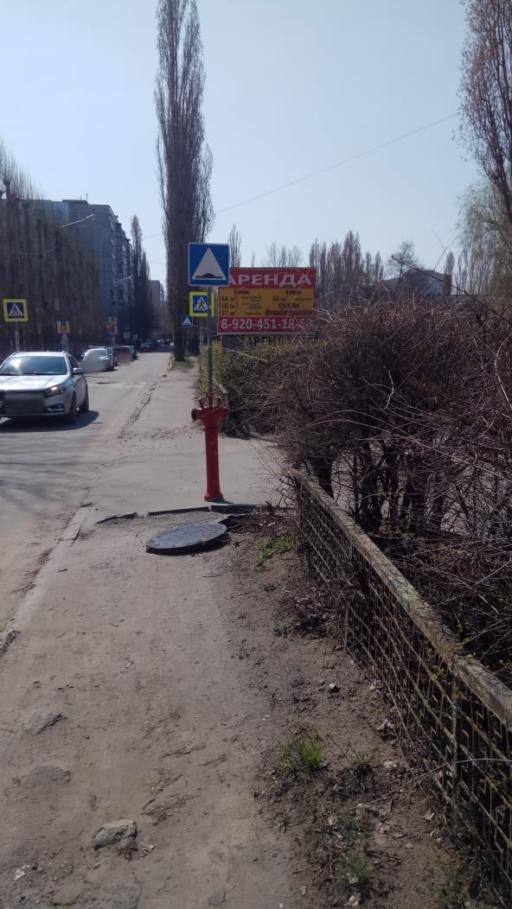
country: RU
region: Voronezj
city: Podgornoye
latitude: 51.7097
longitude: 39.1548
